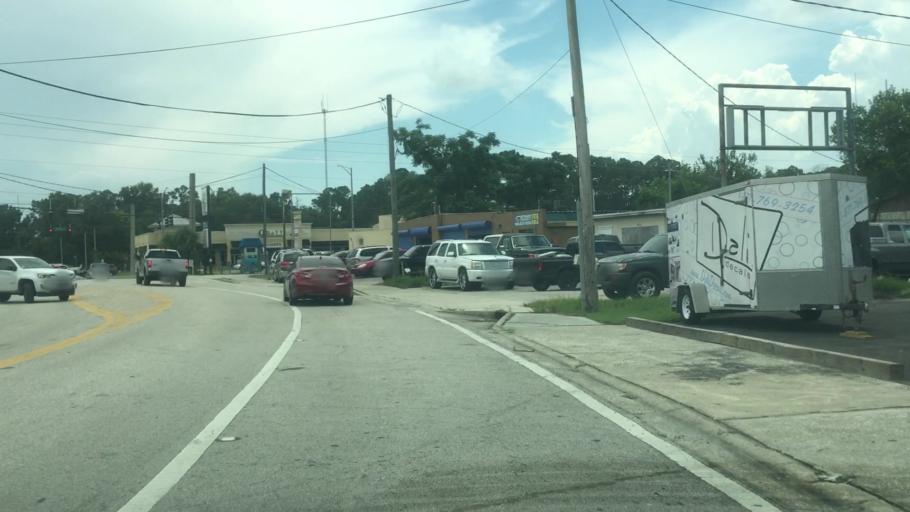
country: US
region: Florida
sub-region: Duval County
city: Jacksonville
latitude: 30.2877
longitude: -81.5486
